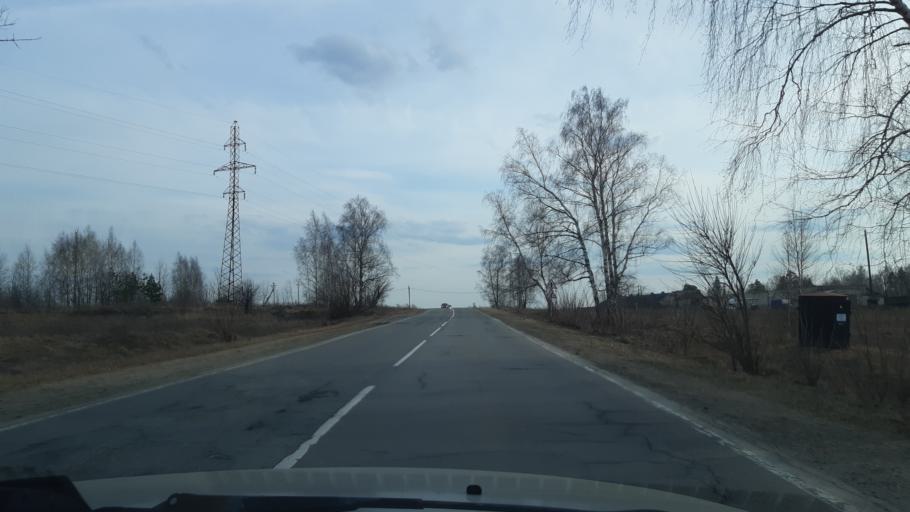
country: RU
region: Vladimir
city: Luknovo
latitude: 56.2021
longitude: 42.0334
